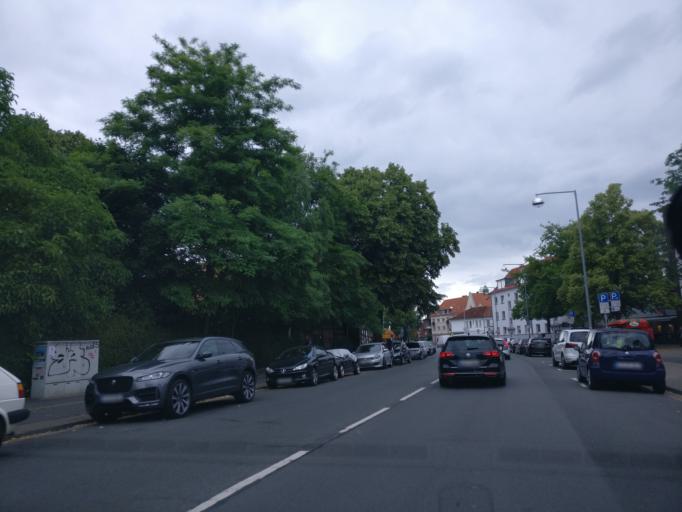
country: DE
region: Lower Saxony
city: Laatzen
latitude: 52.3595
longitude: 9.8274
